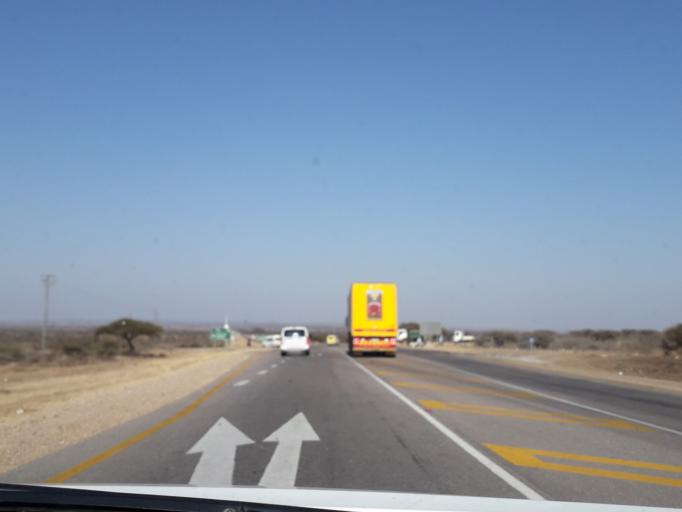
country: ZA
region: Limpopo
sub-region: Capricorn District Municipality
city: Mankoeng
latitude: -23.7570
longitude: 29.6723
